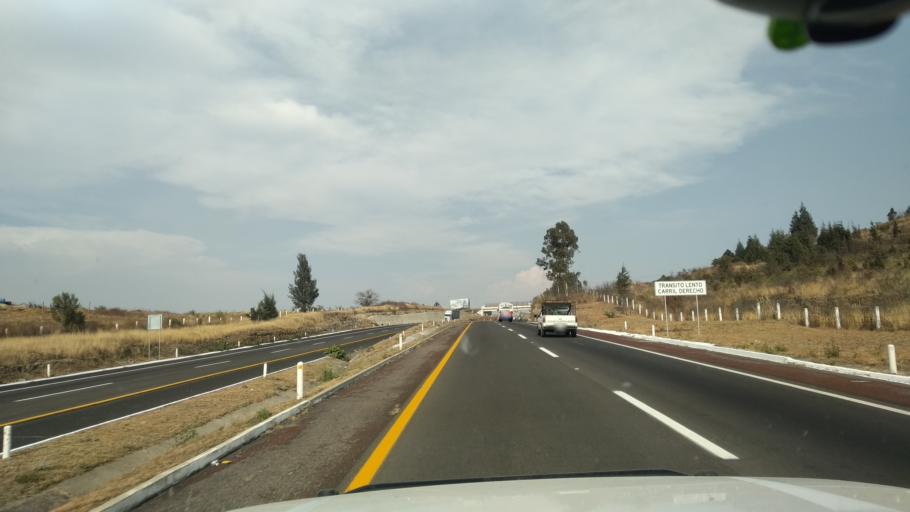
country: MX
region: Puebla
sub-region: Santa Isabel Cholula
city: San Pablo Ahuatempa
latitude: 18.9768
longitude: -98.3612
